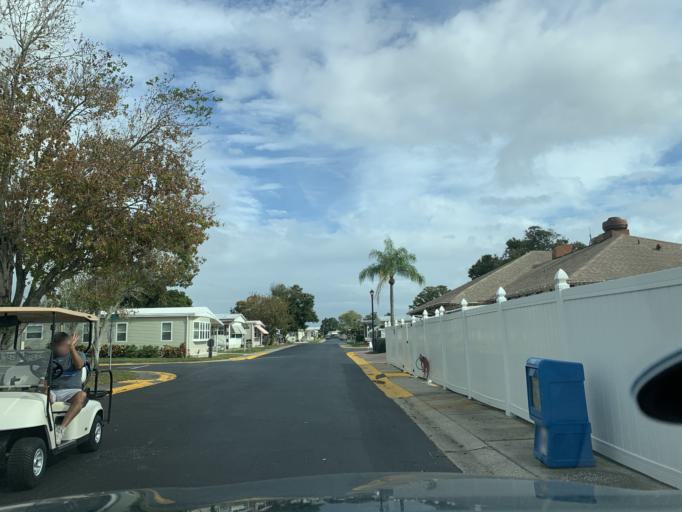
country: US
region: Florida
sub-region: Pinellas County
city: Ridgecrest
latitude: 27.8820
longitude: -82.7911
